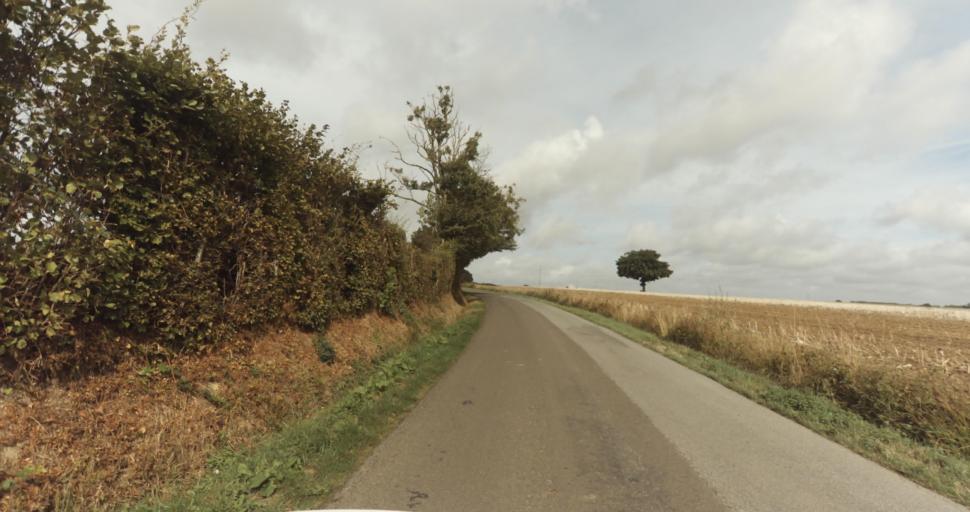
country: FR
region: Lower Normandy
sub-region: Departement de l'Orne
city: Gace
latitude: 48.8423
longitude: 0.3760
